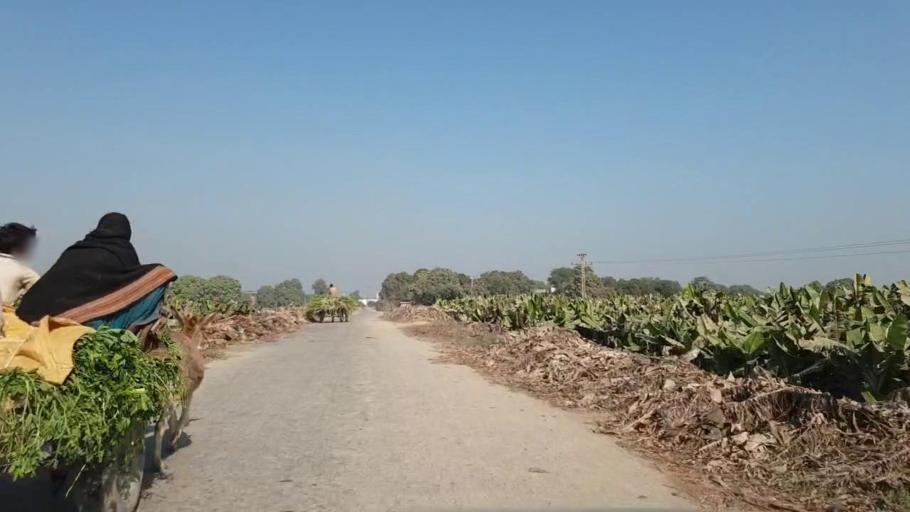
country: PK
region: Sindh
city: Matiari
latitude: 25.5957
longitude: 68.6011
